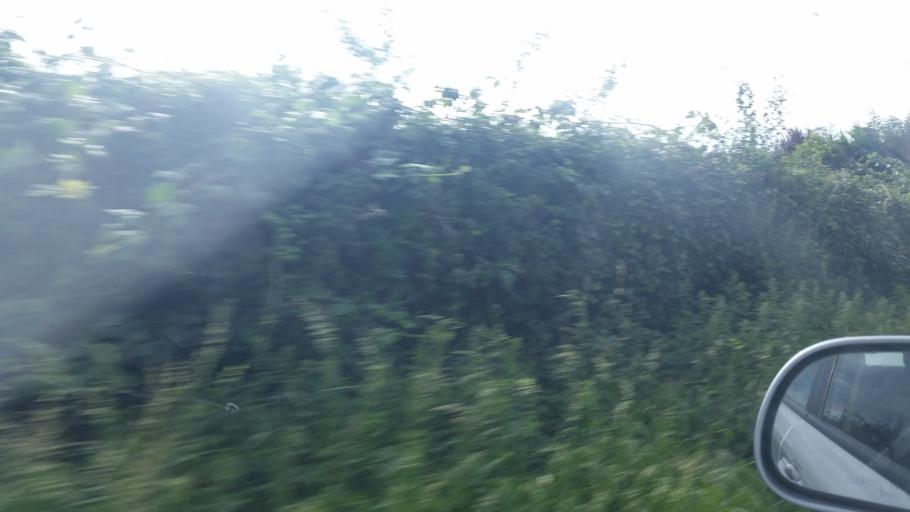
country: IE
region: Leinster
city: Donaghmede
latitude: 53.4118
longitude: -6.1602
